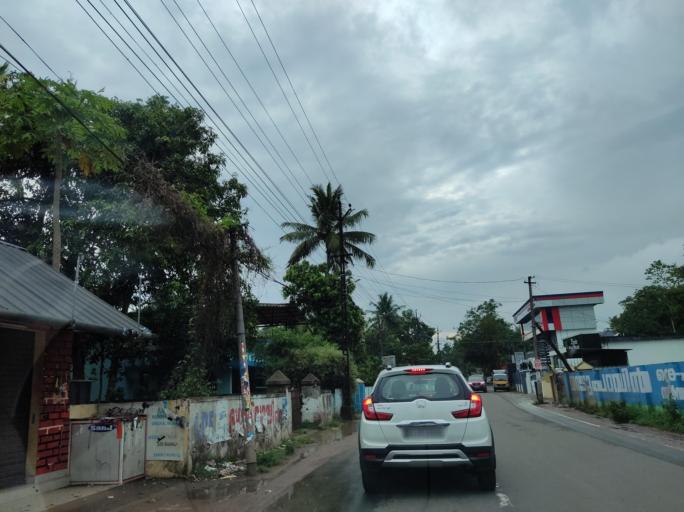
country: IN
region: Kerala
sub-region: Alappuzha
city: Mavelikara
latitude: 9.2499
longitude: 76.4922
